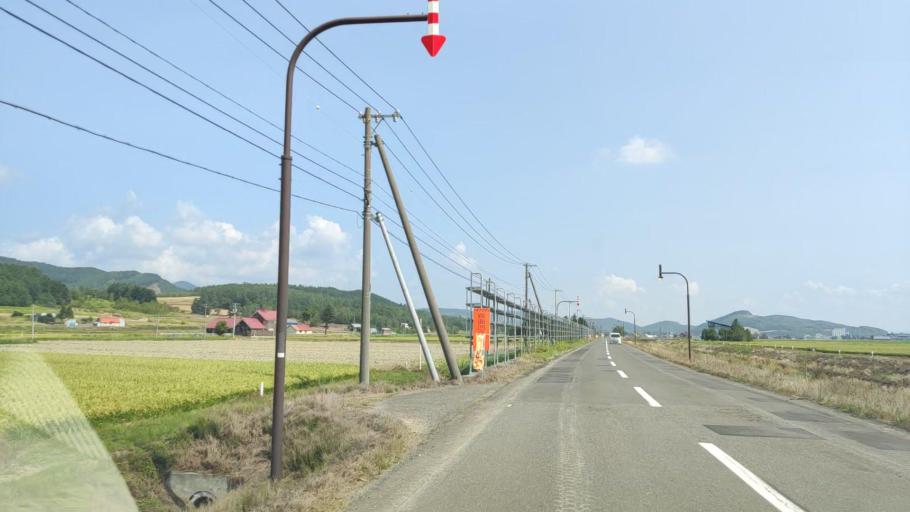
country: JP
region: Hokkaido
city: Shimo-furano
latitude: 43.3728
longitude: 142.3884
